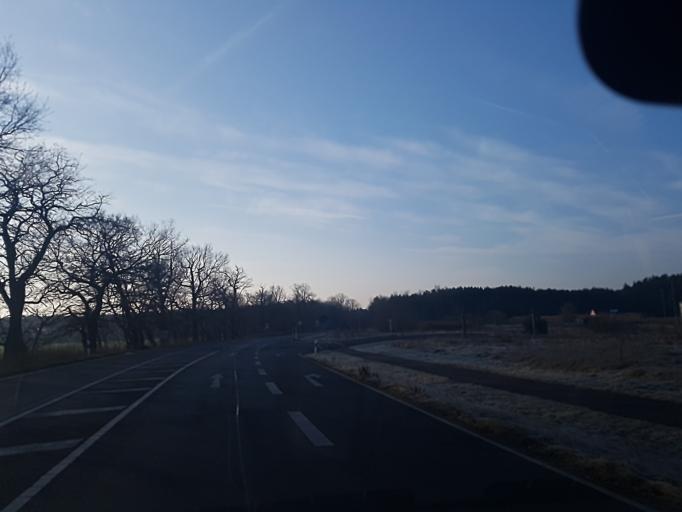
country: DE
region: Brandenburg
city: Golzow
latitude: 52.2672
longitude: 12.5997
